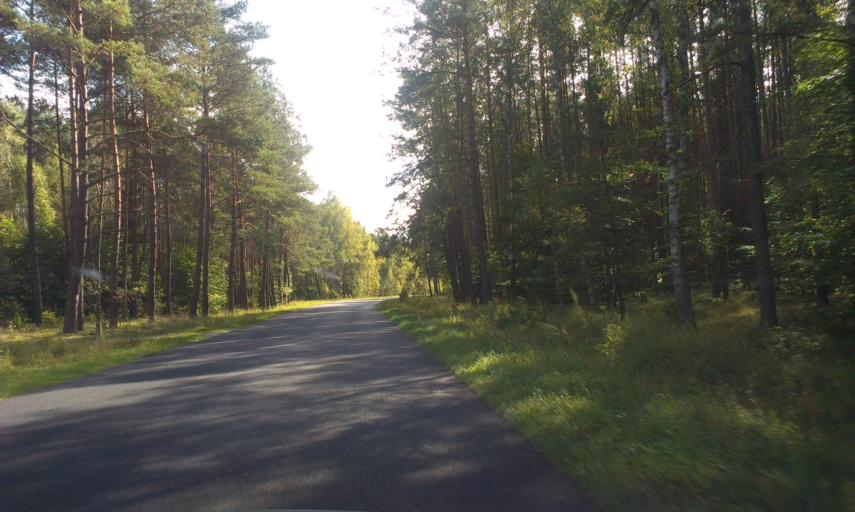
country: PL
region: Greater Poland Voivodeship
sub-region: Powiat zlotowski
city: Okonek
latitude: 53.5285
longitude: 16.9583
